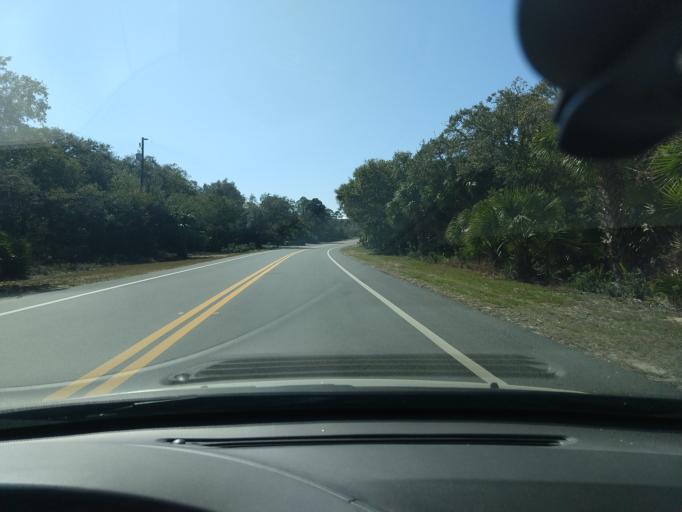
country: US
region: Florida
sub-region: Gulf County
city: Port Saint Joe
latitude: 29.6807
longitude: -85.2281
